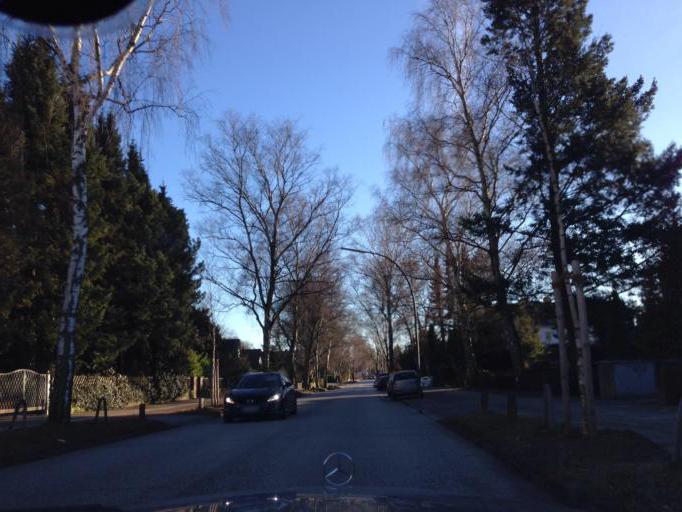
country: DE
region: Hamburg
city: Farmsen-Berne
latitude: 53.6187
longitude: 10.1350
